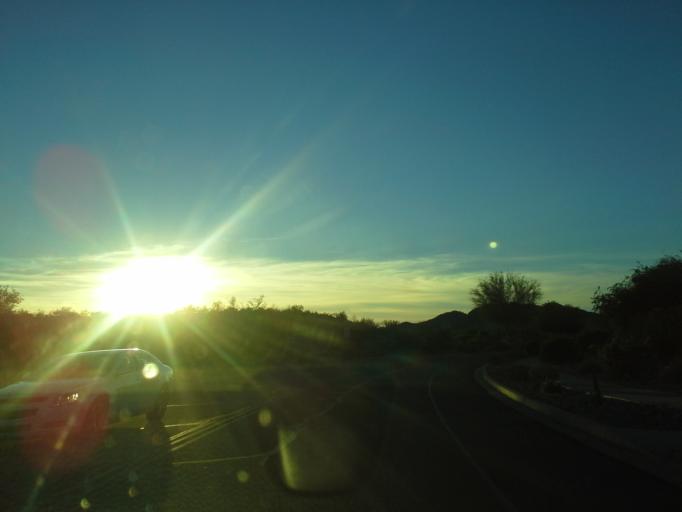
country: US
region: Arizona
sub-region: Pinal County
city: Apache Junction
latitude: 33.3755
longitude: -111.4617
